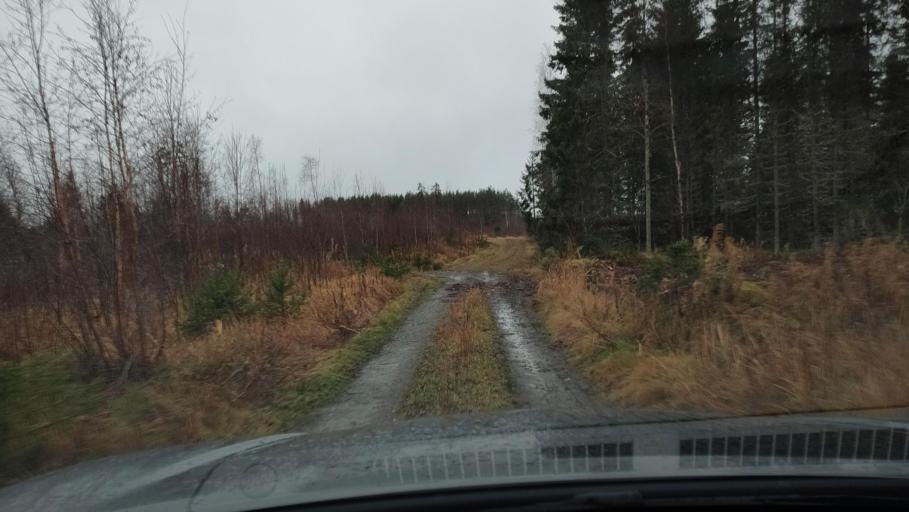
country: FI
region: Southern Ostrobothnia
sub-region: Suupohja
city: Karijoki
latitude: 62.2247
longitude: 21.5522
